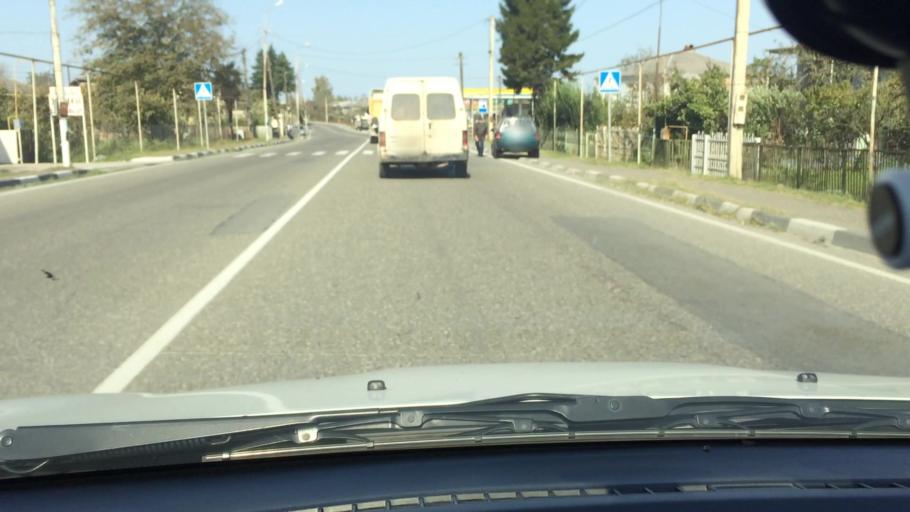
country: GE
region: Guria
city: Lanchkhuti
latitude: 42.0812
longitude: 42.0496
